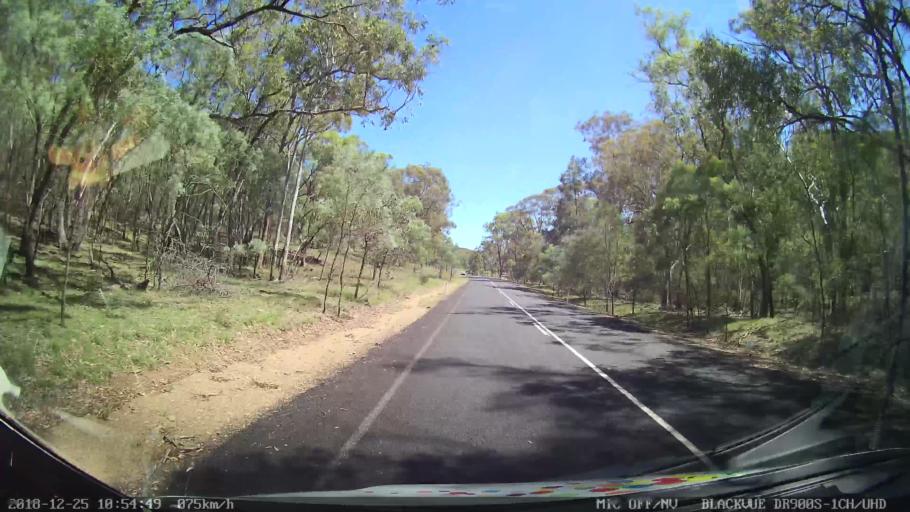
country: AU
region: New South Wales
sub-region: Upper Hunter Shire
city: Merriwa
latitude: -32.4058
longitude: 150.2735
